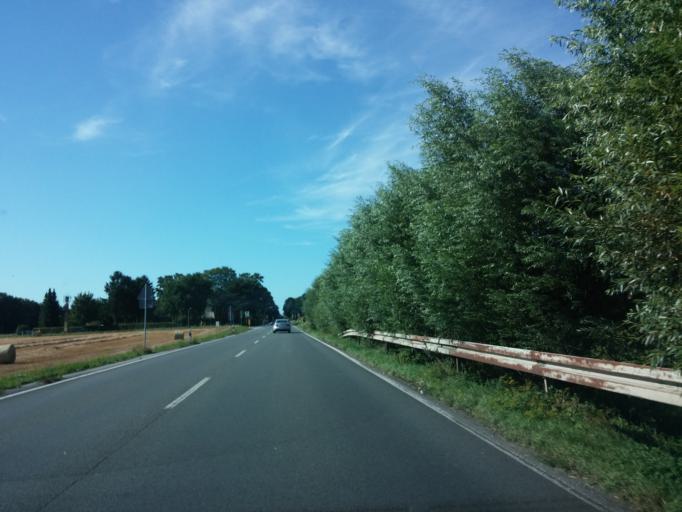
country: DE
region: North Rhine-Westphalia
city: Dorsten
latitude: 51.6459
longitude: 6.9860
